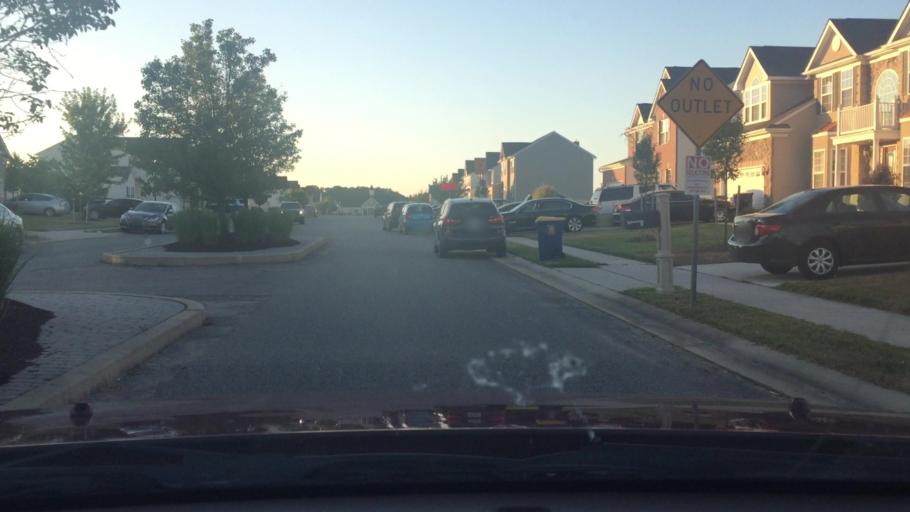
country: US
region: Delaware
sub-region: Kent County
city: Woodside East
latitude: 39.0519
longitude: -75.5219
